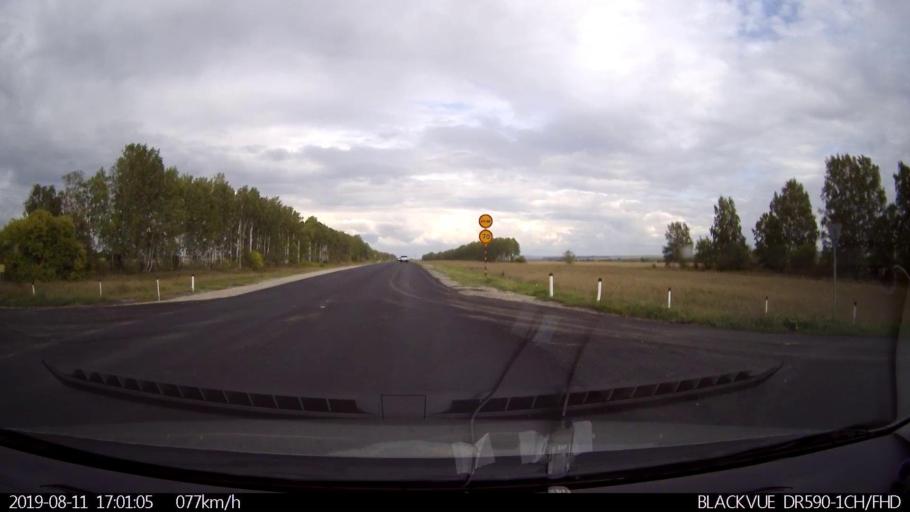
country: RU
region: Ulyanovsk
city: Mayna
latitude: 54.3089
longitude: 47.6910
